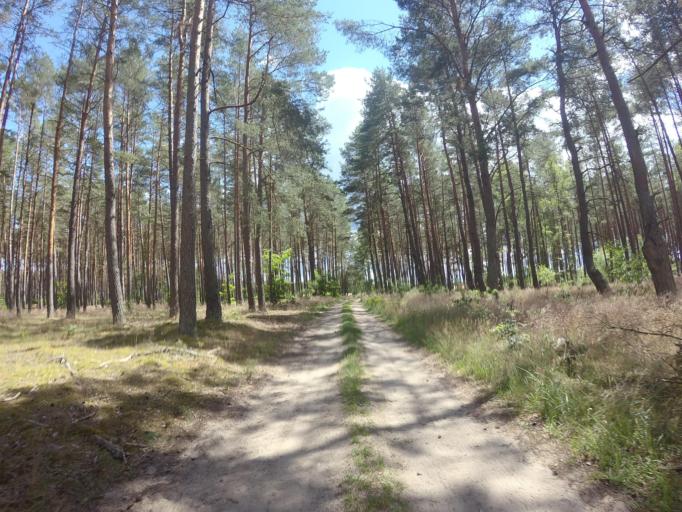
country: PL
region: West Pomeranian Voivodeship
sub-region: Powiat choszczenski
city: Drawno
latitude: 53.1888
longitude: 15.8578
